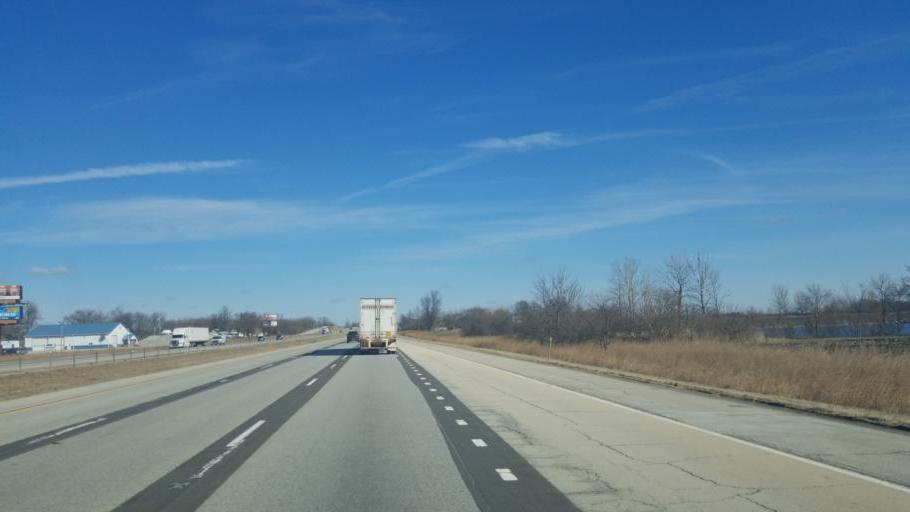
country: US
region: Illinois
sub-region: Sangamon County
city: Divernon
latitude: 39.6202
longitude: -89.6468
